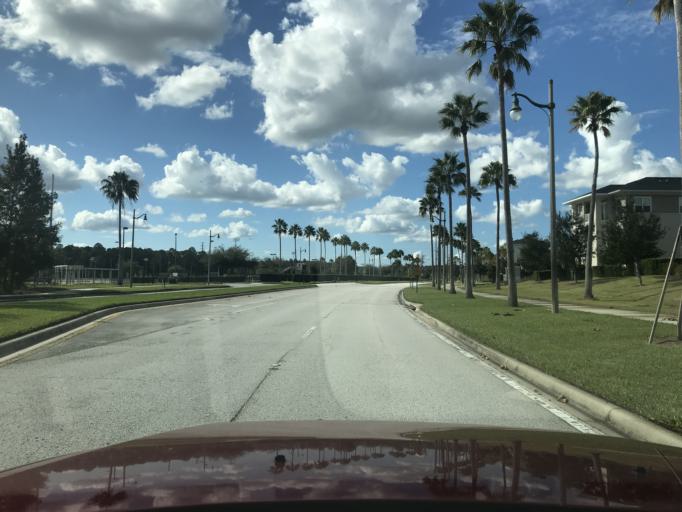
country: US
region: Florida
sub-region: Osceola County
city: Celebration
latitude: 28.3006
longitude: -81.5680
